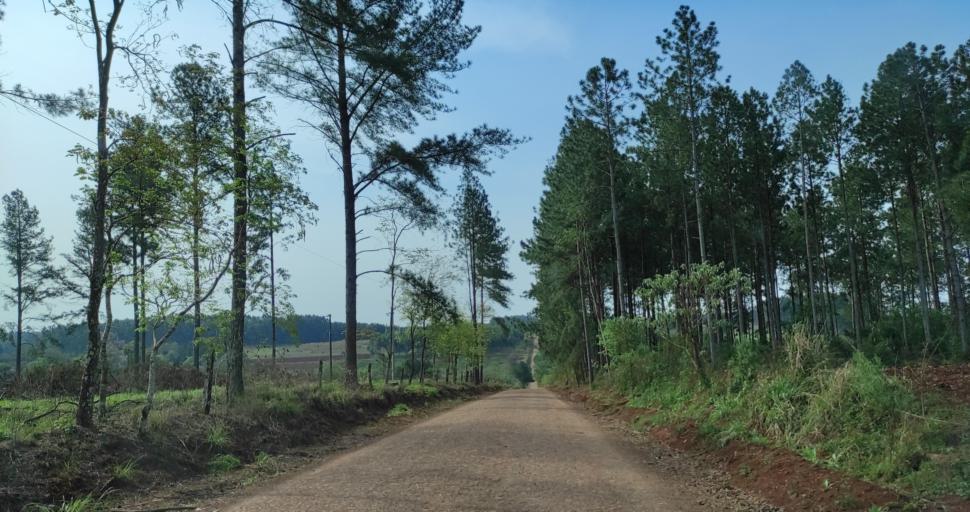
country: AR
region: Misiones
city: Garuhape
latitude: -26.8746
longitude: -55.0059
